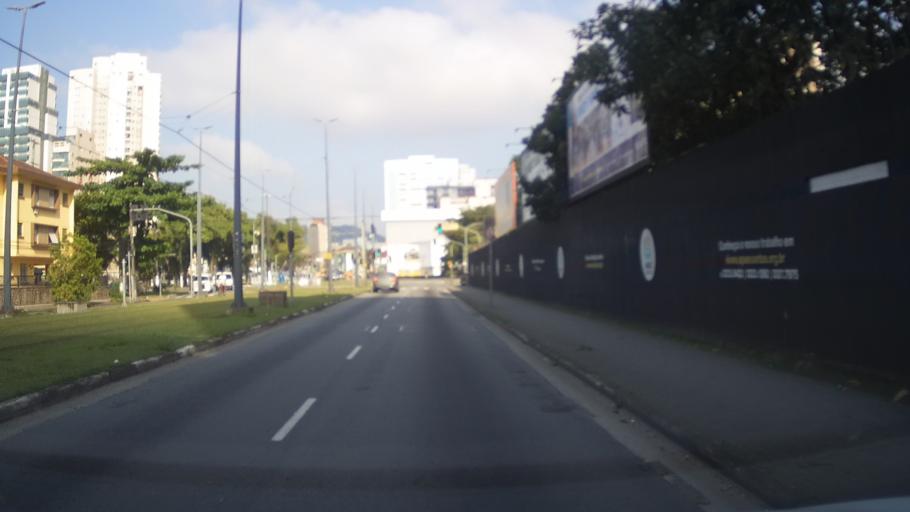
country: BR
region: Sao Paulo
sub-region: Santos
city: Santos
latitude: -23.9574
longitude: -46.3255
